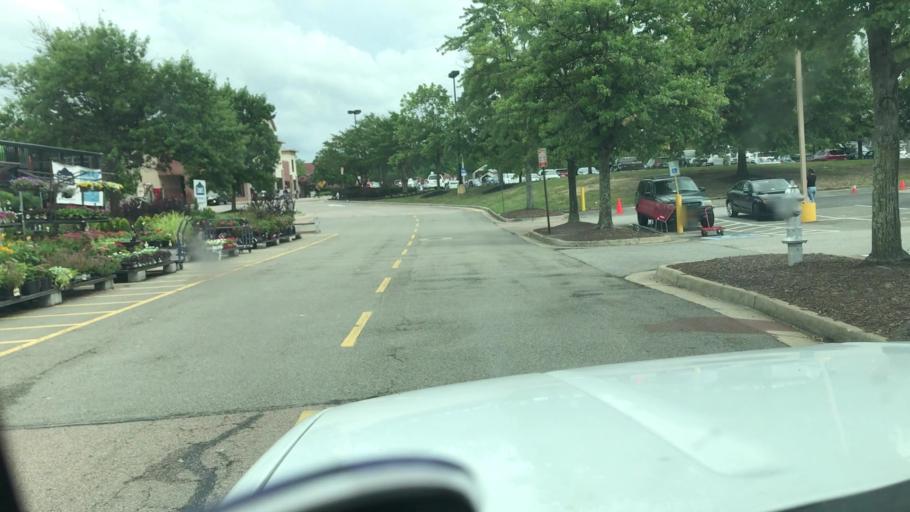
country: US
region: Virginia
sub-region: Henrico County
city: Laurel
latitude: 37.6411
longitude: -77.5567
